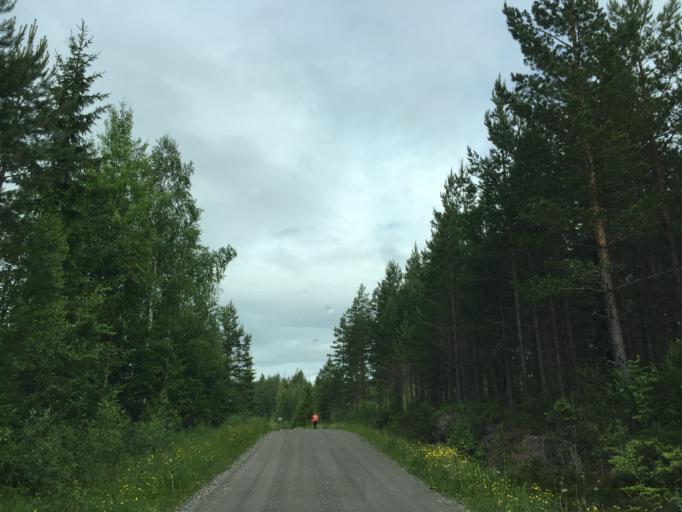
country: NO
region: Hedmark
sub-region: Kongsvinger
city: Kongsvinger
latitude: 60.1704
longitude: 11.9714
